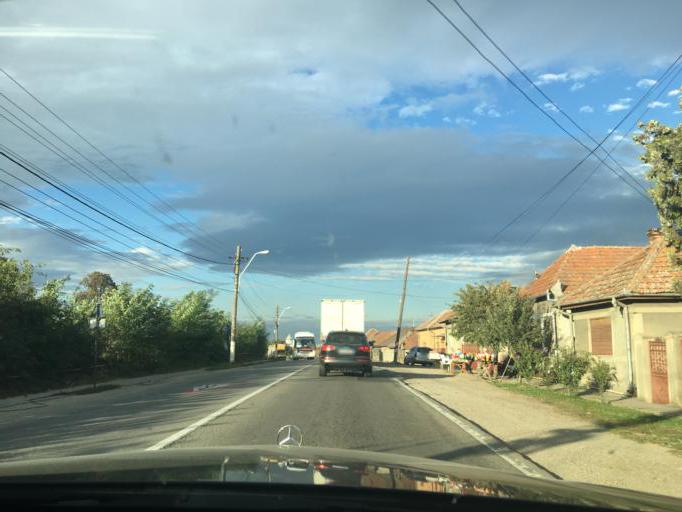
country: RO
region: Alba
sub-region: Oras Teius
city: Teius
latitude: 46.1999
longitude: 23.6707
